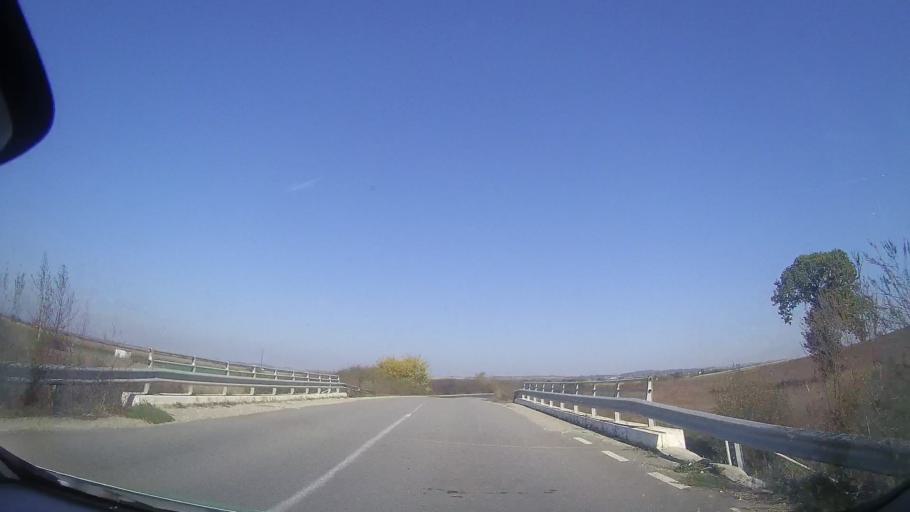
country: RO
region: Timis
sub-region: Comuna Balint
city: Balint
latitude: 45.7851
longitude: 21.8481
